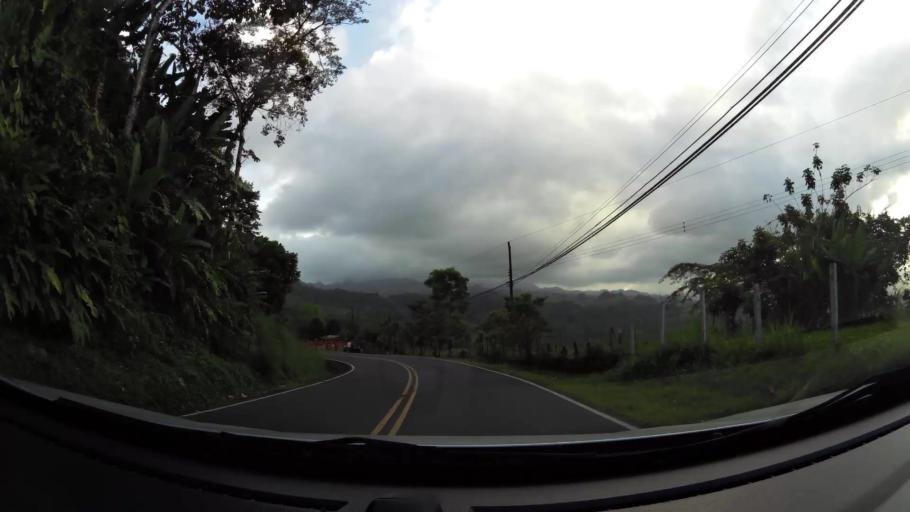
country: CR
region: Limon
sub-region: Canton de Siquirres
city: Siquirres
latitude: 9.9954
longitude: -83.5737
